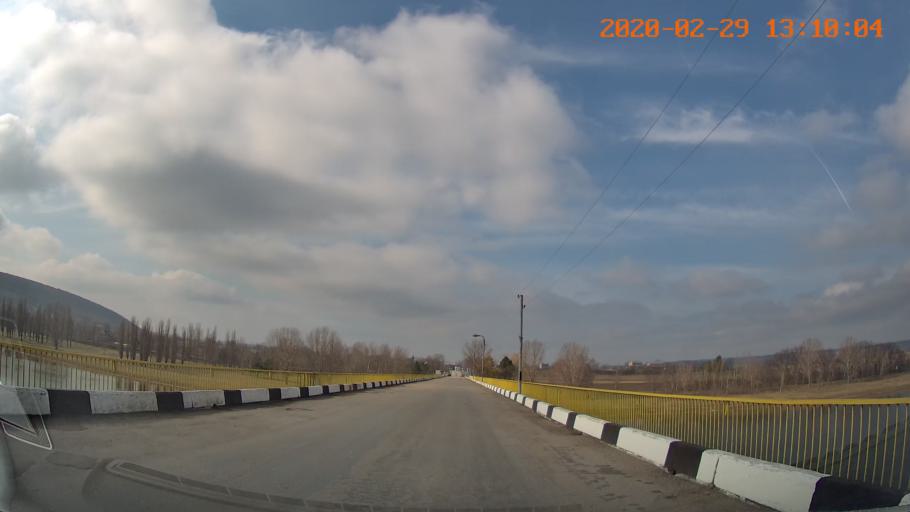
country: MD
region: Telenesti
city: Camenca
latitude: 48.0118
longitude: 28.7017
